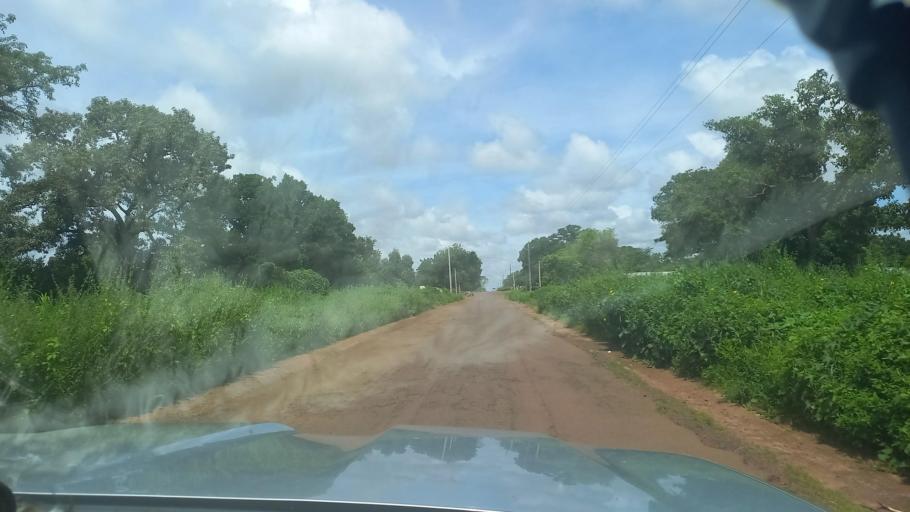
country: GM
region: Lower River
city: Kaiaf
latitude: 13.2194
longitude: -15.5420
